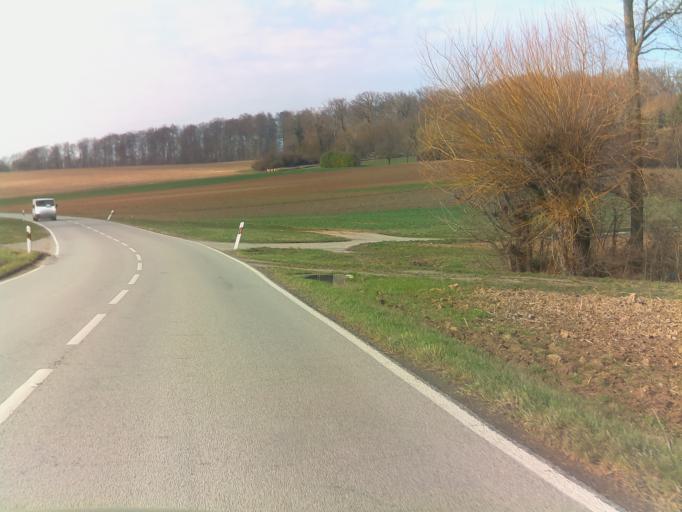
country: DE
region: Baden-Wuerttemberg
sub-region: Regierungsbezirk Stuttgart
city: Gemmingen
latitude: 49.1652
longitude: 8.9758
